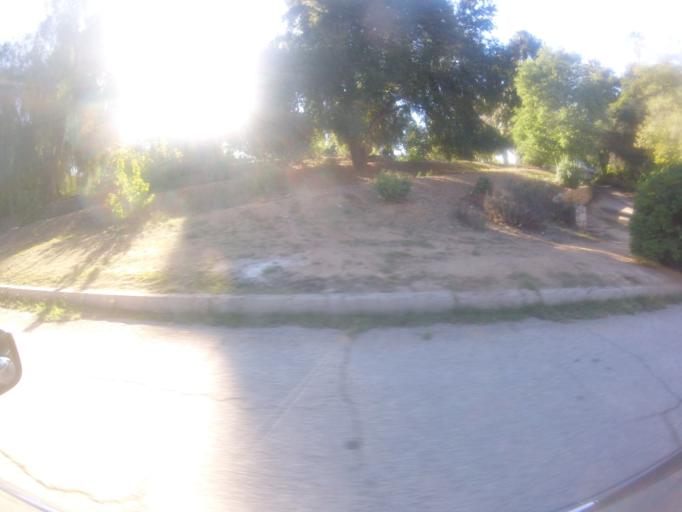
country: US
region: California
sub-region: San Bernardino County
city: Redlands
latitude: 34.0306
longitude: -117.1829
